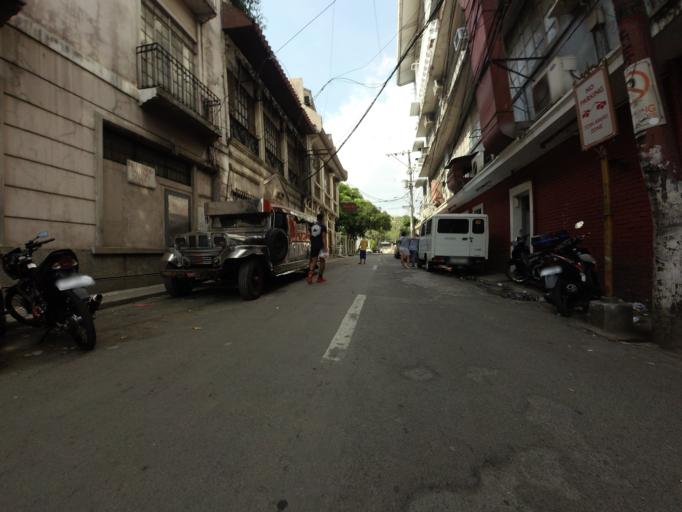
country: PH
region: Metro Manila
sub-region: City of Manila
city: Port Area
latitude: 14.5929
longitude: 120.9729
